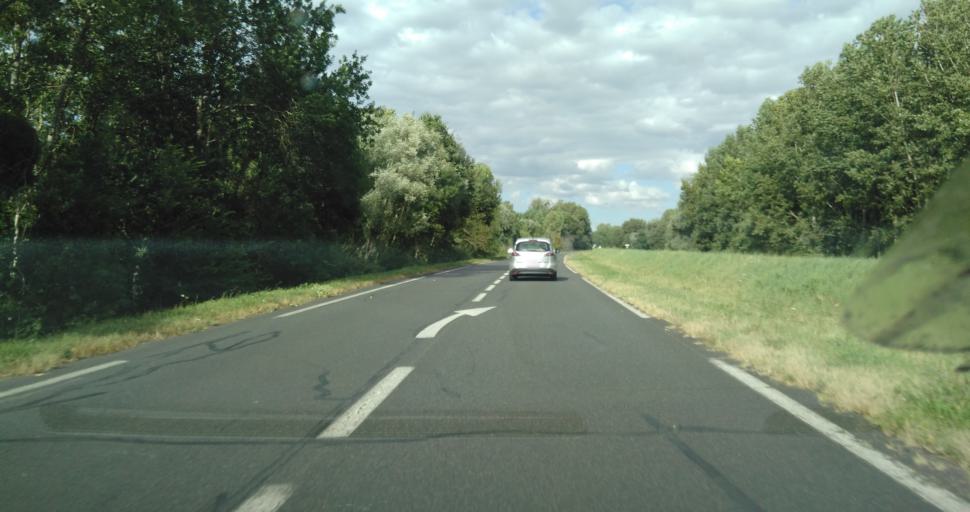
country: FR
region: Centre
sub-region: Departement d'Indre-et-Loire
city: Huismes
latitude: 47.2810
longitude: 0.3169
